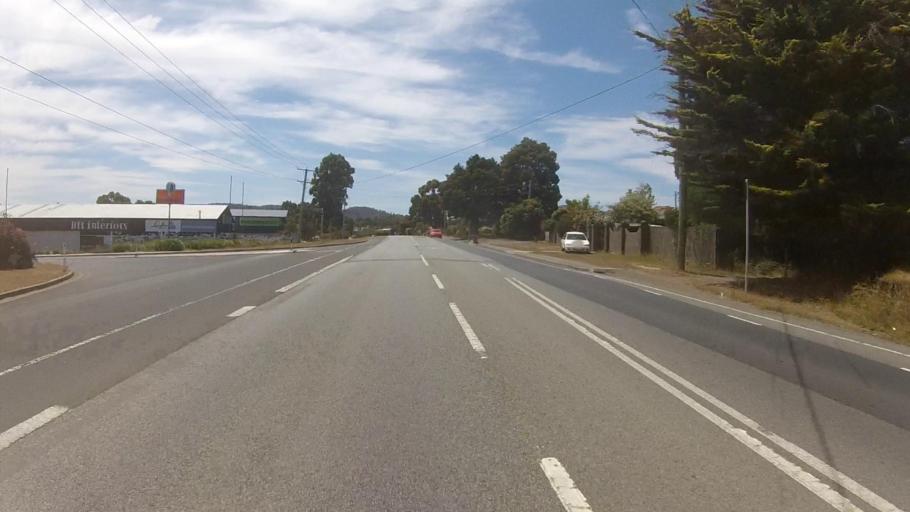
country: AU
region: Tasmania
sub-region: Kingborough
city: Kingston
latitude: -42.9830
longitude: 147.2948
